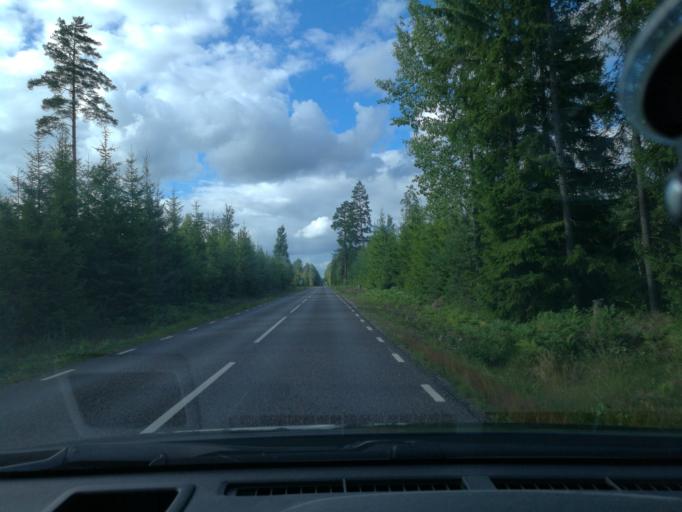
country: SE
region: Kronoberg
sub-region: Vaxjo Kommun
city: Braas
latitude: 57.0681
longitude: 15.0091
